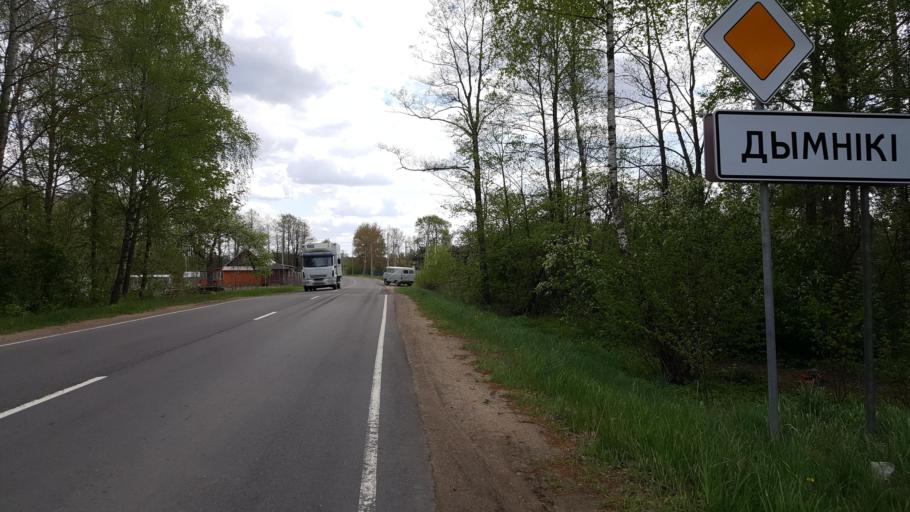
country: BY
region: Brest
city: Zhabinka
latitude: 52.3970
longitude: 24.0896
